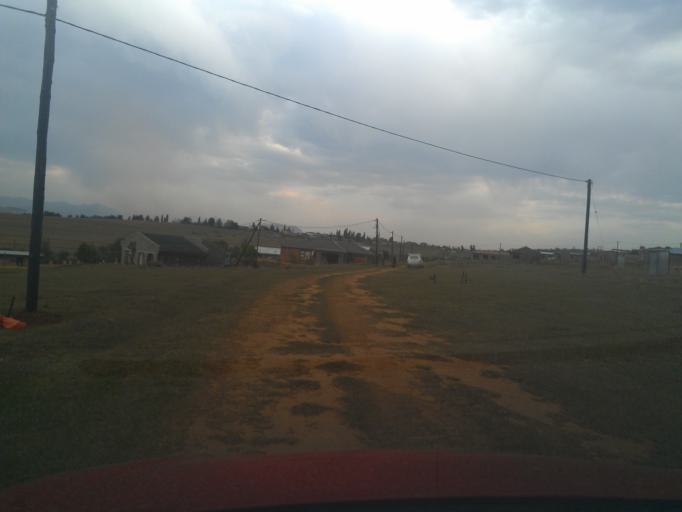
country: LS
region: Berea
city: Teyateyaneng
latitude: -29.1285
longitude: 27.7636
